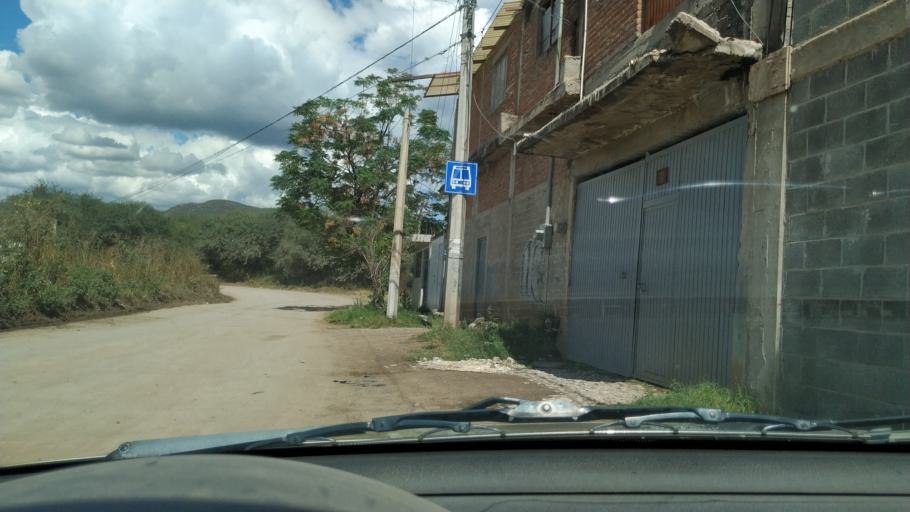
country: MX
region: Guanajuato
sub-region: Leon
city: Medina
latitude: 21.1413
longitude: -101.6285
